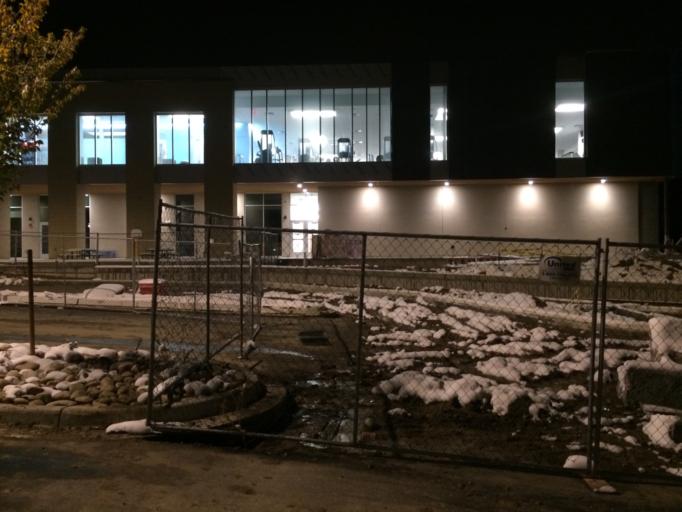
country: US
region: Colorado
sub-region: Boulder County
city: Superior
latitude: 39.9745
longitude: -105.1583
